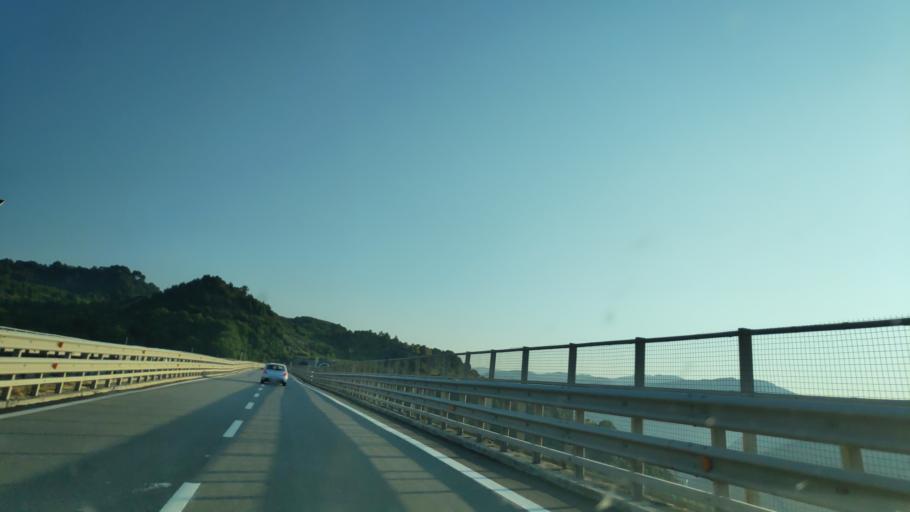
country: IT
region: Calabria
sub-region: Provincia di Cosenza
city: Carpanzano
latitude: 39.1481
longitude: 16.2821
